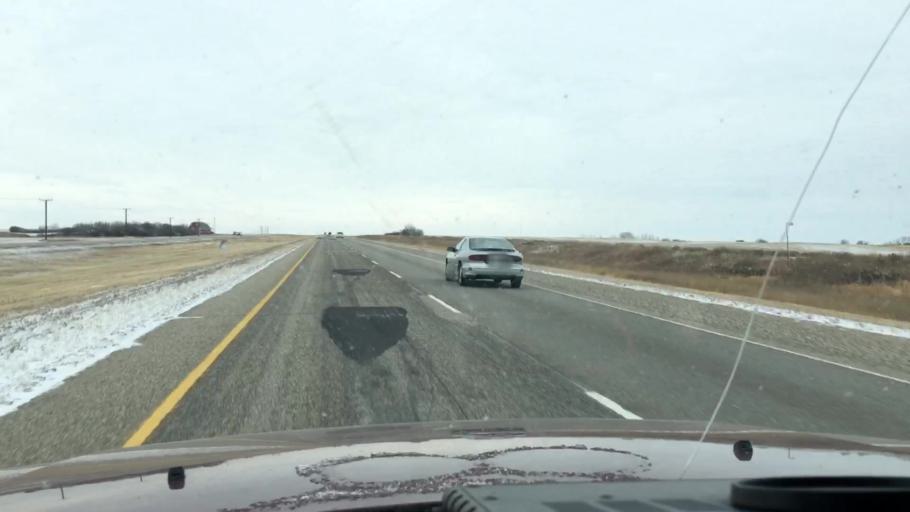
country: CA
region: Saskatchewan
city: Watrous
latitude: 51.4239
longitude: -106.1956
